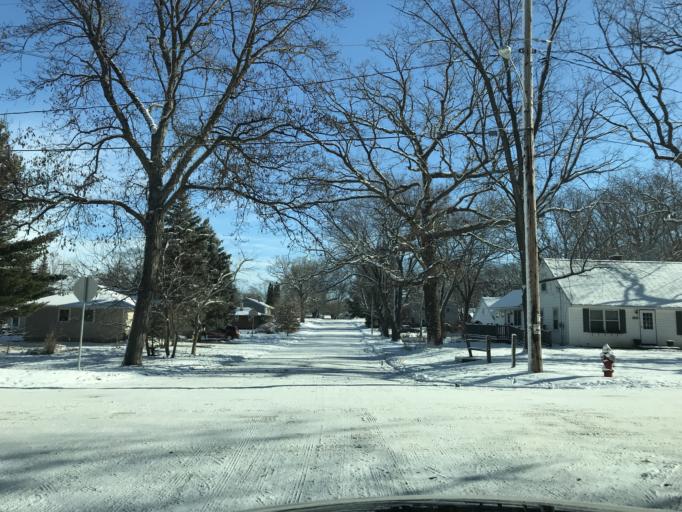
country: US
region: Wisconsin
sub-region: Dane County
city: Monona
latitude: 43.0828
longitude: -89.3193
